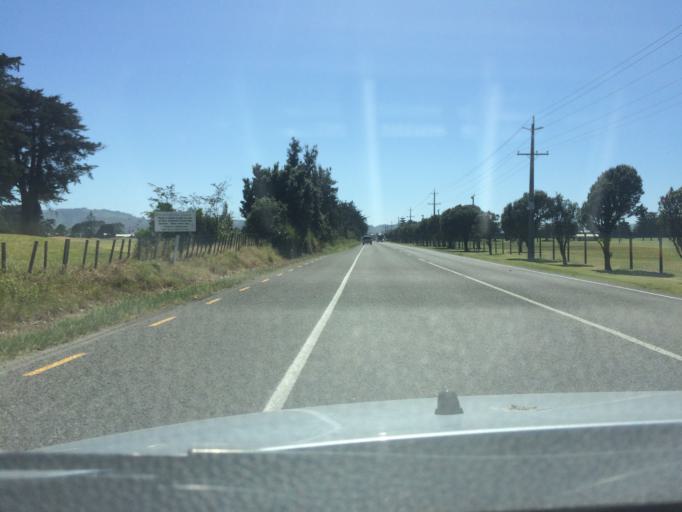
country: NZ
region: Gisborne
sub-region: Gisborne District
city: Gisborne
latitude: -38.6711
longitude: 177.9925
